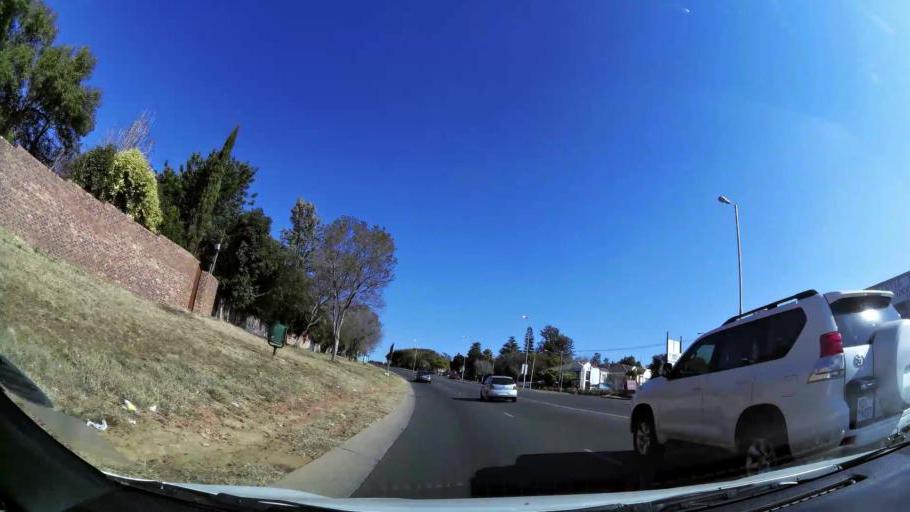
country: ZA
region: Gauteng
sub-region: City of Tshwane Metropolitan Municipality
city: Centurion
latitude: -25.8110
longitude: 28.2787
